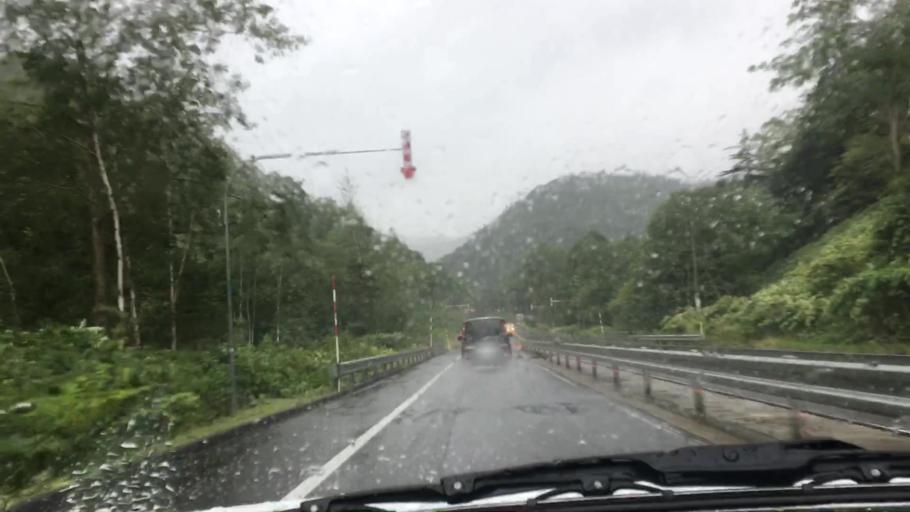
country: JP
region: Hokkaido
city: Otaru
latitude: 42.8451
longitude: 141.0577
